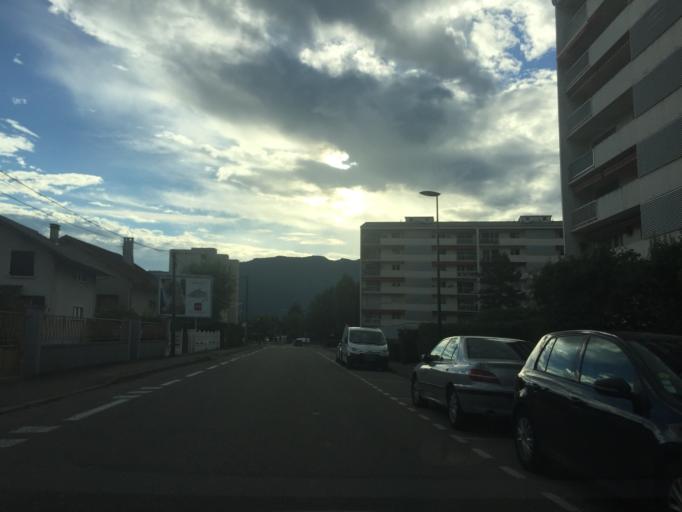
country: FR
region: Rhone-Alpes
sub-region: Departement de la Savoie
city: Aix-les-Bains
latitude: 45.7017
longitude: 5.9114
